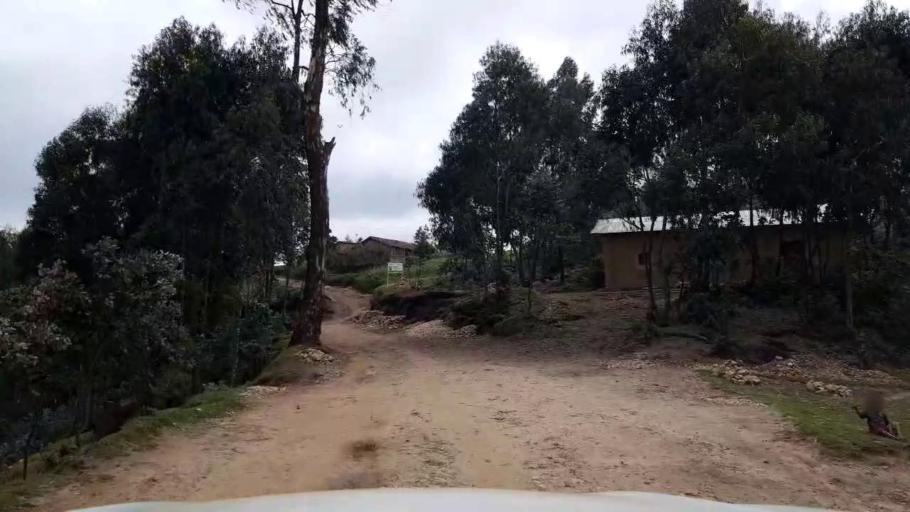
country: RW
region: Western Province
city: Kibuye
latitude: -1.9424
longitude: 29.4674
